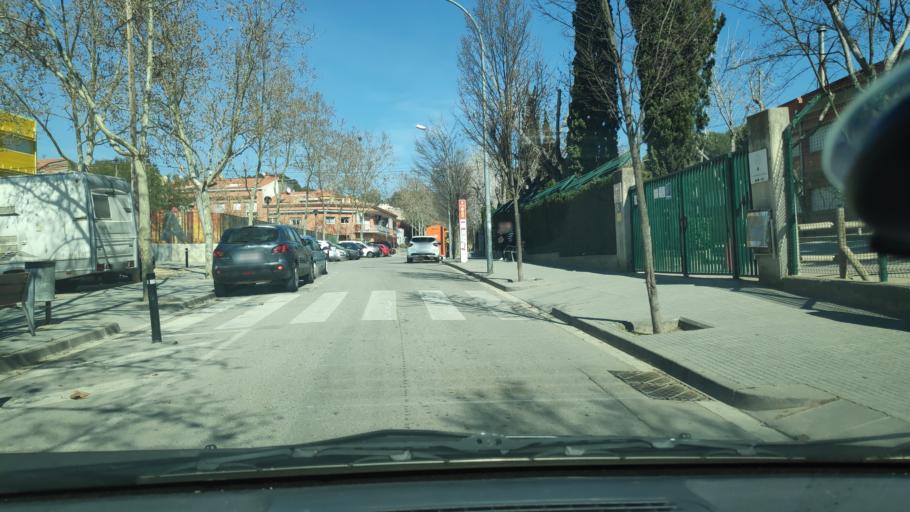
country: ES
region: Catalonia
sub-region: Provincia de Barcelona
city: Rubi
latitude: 41.4984
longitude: 2.0456
